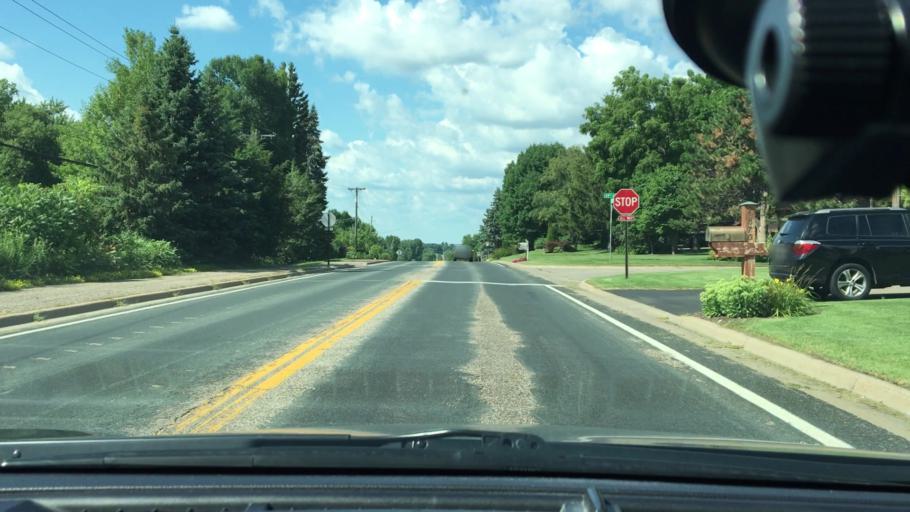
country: US
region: Minnesota
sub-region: Hennepin County
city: New Hope
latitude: 45.0433
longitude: -93.4209
